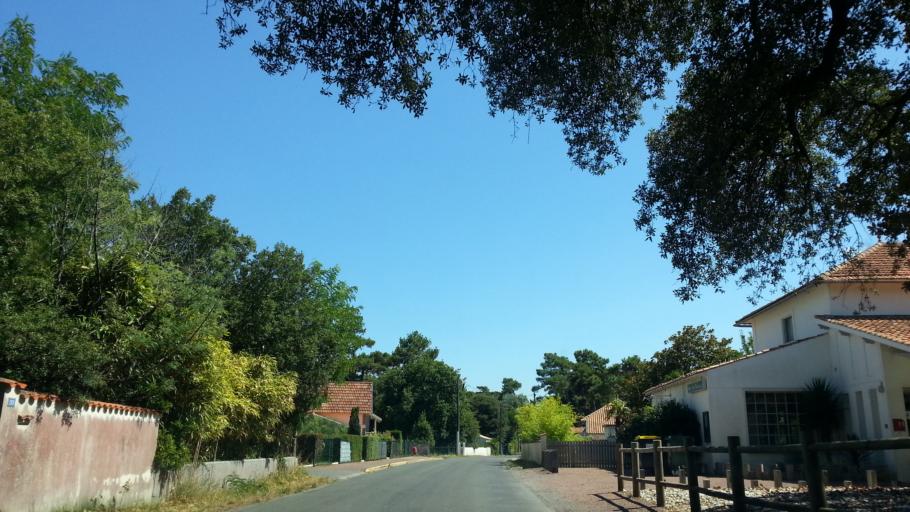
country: FR
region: Poitou-Charentes
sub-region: Departement de la Charente-Maritime
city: Dolus-d'Oleron
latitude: 45.8828
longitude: -1.2558
